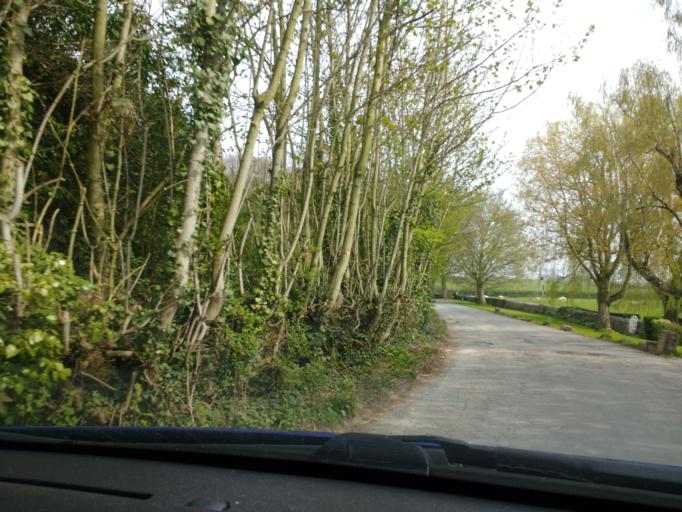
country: GB
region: England
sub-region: Lancashire
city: Lancaster
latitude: 54.0071
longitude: -2.8229
